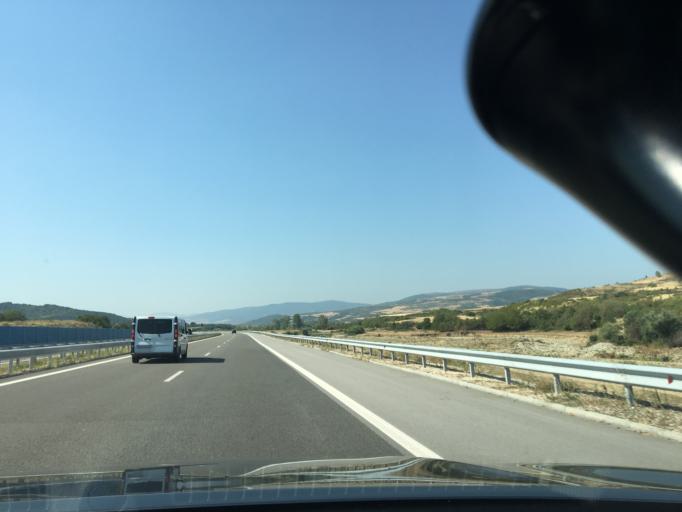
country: BG
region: Kyustendil
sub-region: Obshtina Dupnitsa
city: Dupnitsa
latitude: 42.2279
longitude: 23.0802
